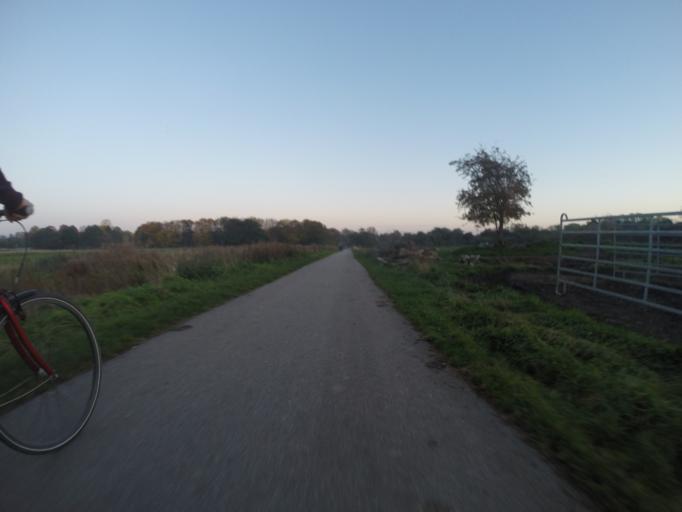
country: DK
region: Capital Region
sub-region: Hoje-Taastrup Kommune
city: Taastrup
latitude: 55.6577
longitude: 12.3253
